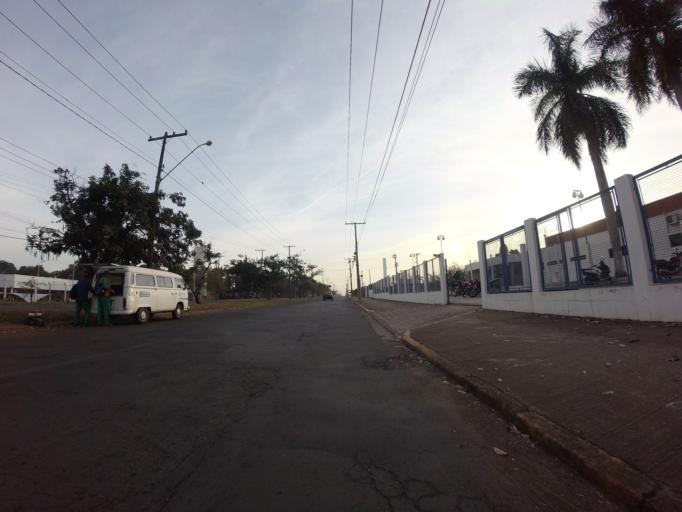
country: BR
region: Sao Paulo
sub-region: Piracicaba
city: Piracicaba
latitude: -22.7367
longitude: -47.5894
